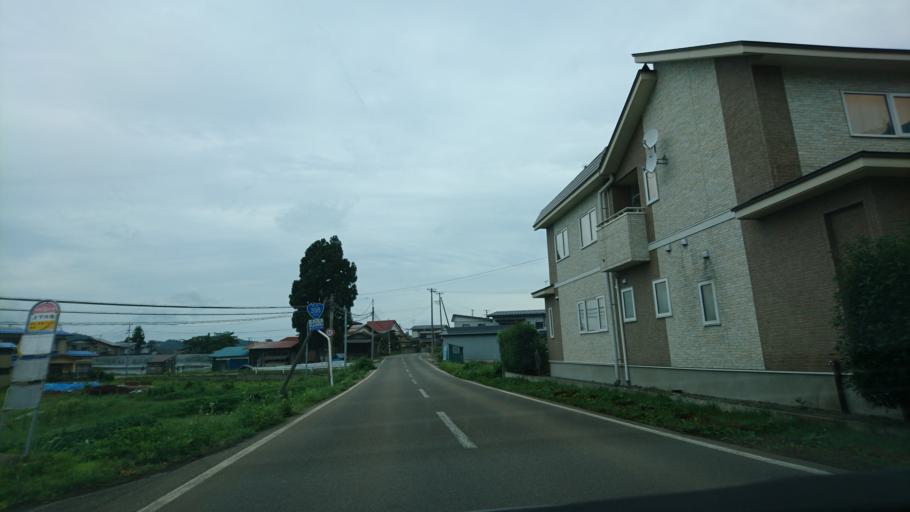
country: JP
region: Akita
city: Yuzawa
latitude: 39.1423
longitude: 140.5771
